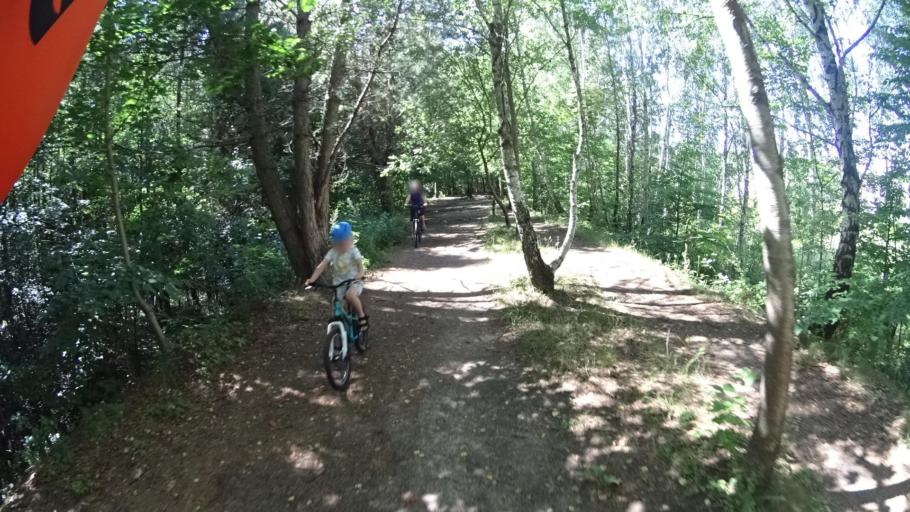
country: PL
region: Masovian Voivodeship
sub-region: Warszawa
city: Kabaty
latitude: 52.1247
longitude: 21.0699
